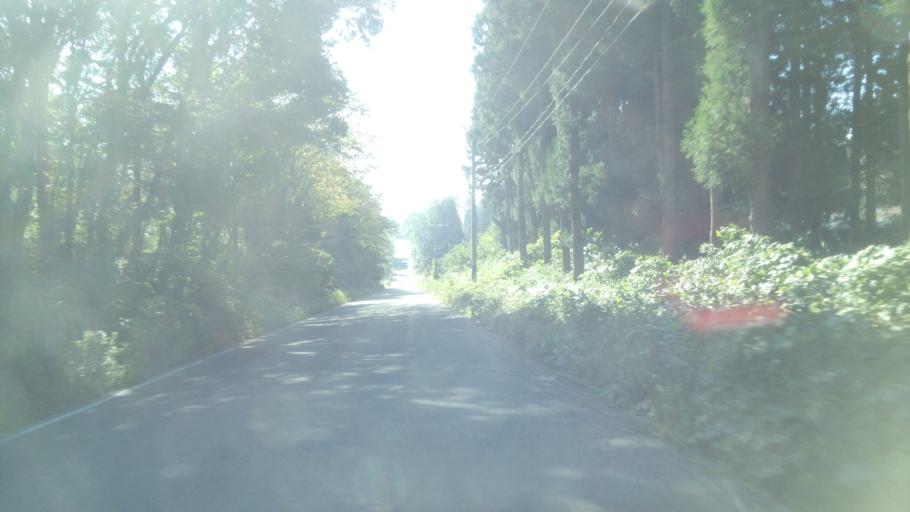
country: JP
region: Fukushima
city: Kitakata
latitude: 37.5986
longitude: 139.9437
